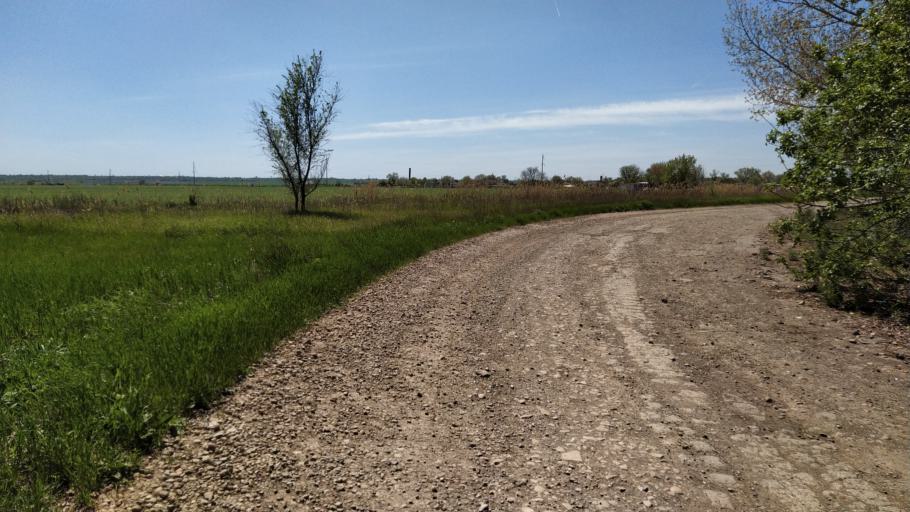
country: RU
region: Rostov
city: Kuleshovka
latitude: 47.0573
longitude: 39.6248
